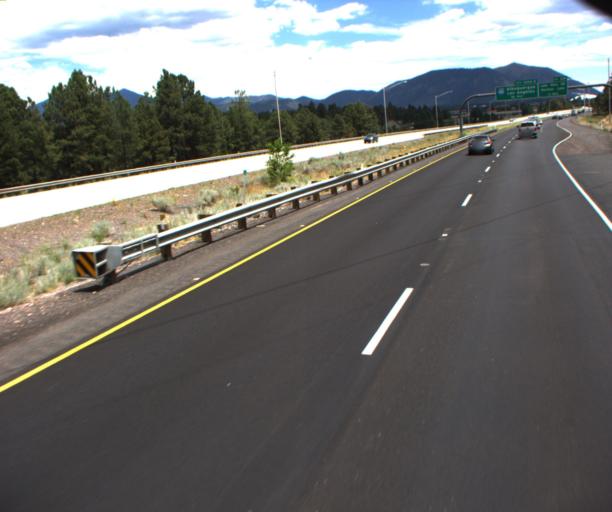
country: US
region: Arizona
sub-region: Coconino County
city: Flagstaff
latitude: 35.1630
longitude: -111.6737
